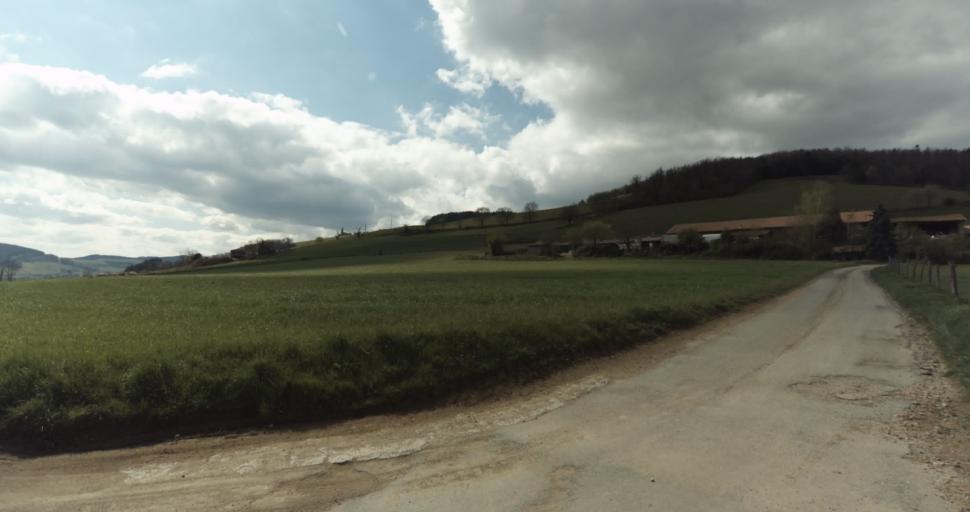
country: FR
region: Rhone-Alpes
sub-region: Departement du Rhone
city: Tarare
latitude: 45.9112
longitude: 4.4227
